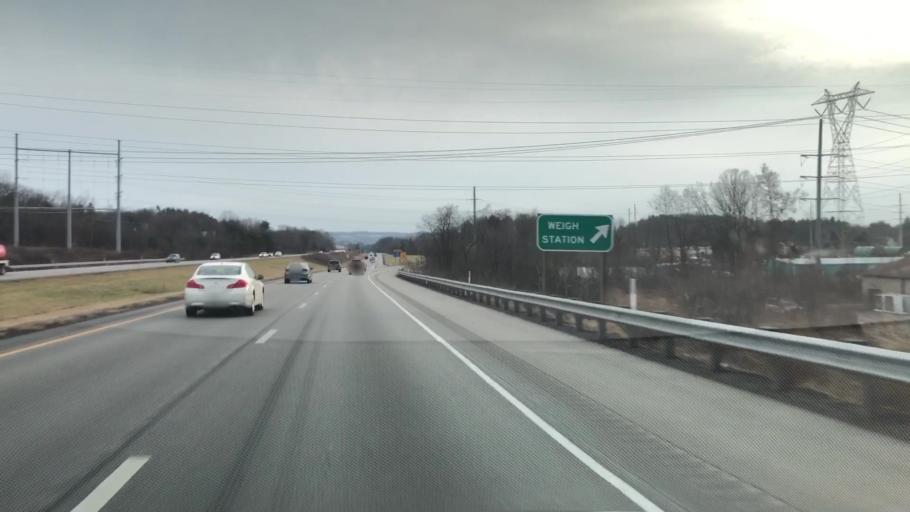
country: US
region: Pennsylvania
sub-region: Butler County
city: Fox Run
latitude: 40.7232
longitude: -80.1019
